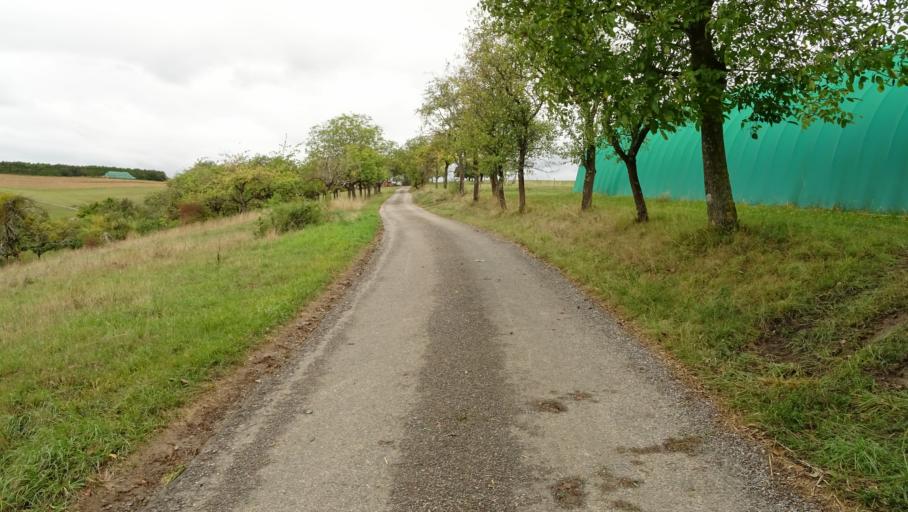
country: DE
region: Baden-Wuerttemberg
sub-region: Karlsruhe Region
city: Fahrenbach
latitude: 49.4015
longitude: 9.1297
